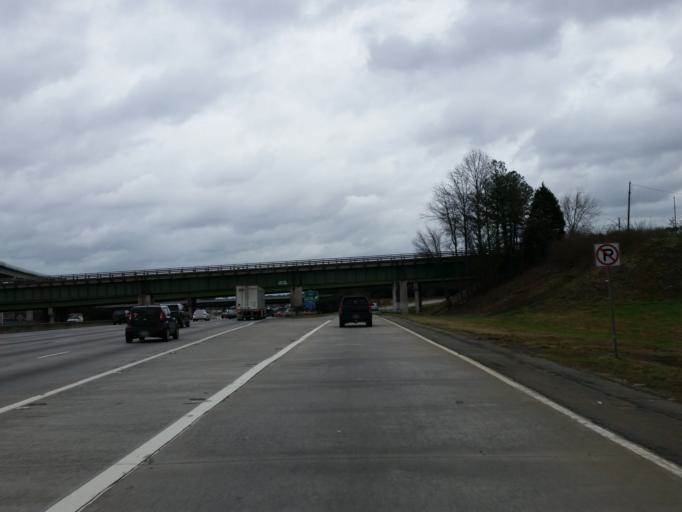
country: US
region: Georgia
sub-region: Cobb County
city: Marietta
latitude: 33.9806
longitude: -84.5378
